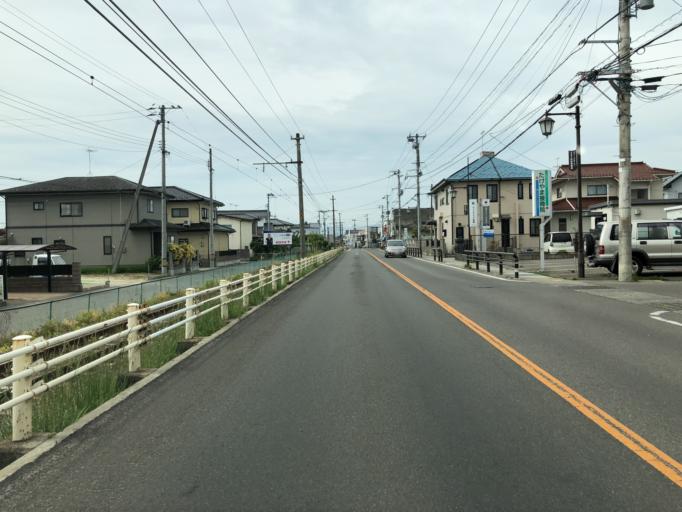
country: JP
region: Fukushima
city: Fukushima-shi
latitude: 37.8081
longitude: 140.4437
